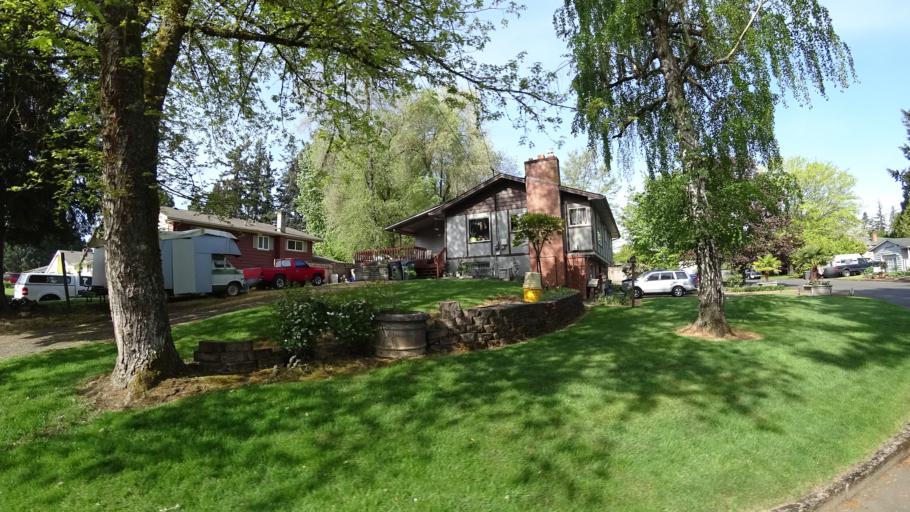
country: US
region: Oregon
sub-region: Washington County
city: Hillsboro
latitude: 45.5240
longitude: -122.9690
